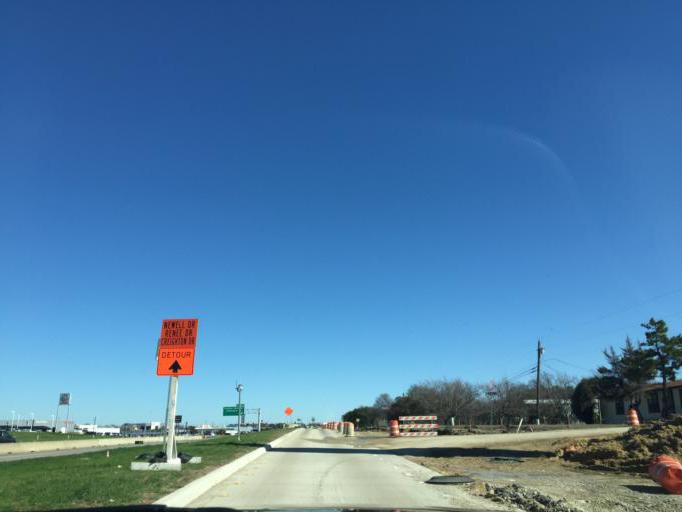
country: US
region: Texas
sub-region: Parker County
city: Hudson Oaks
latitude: 32.7532
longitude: -97.7078
